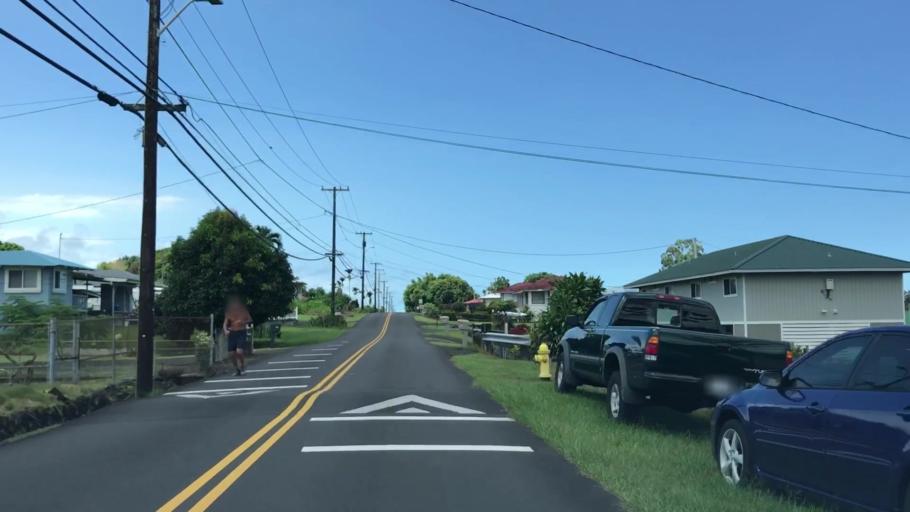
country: US
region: Hawaii
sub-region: Hawaii County
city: Hilo
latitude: 19.6769
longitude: -155.0800
